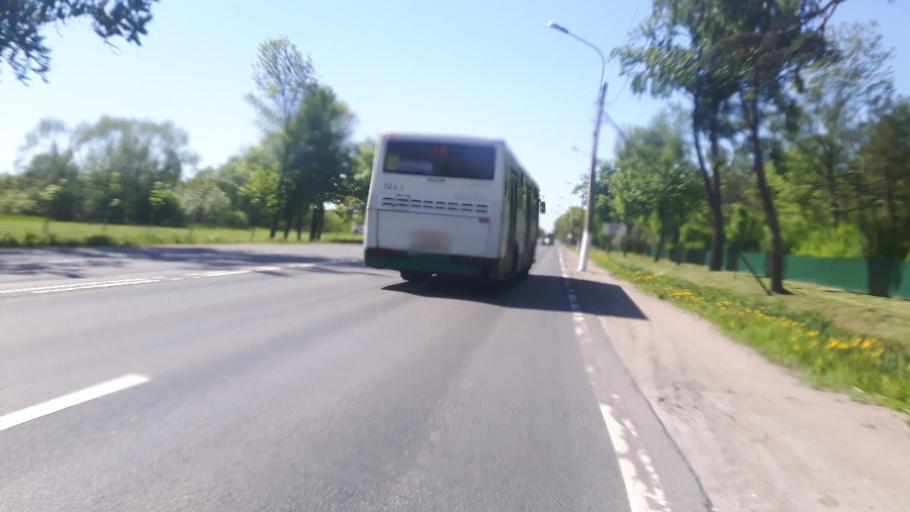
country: RU
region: Leningrad
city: Ol'gino
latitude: 59.8721
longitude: 29.9648
